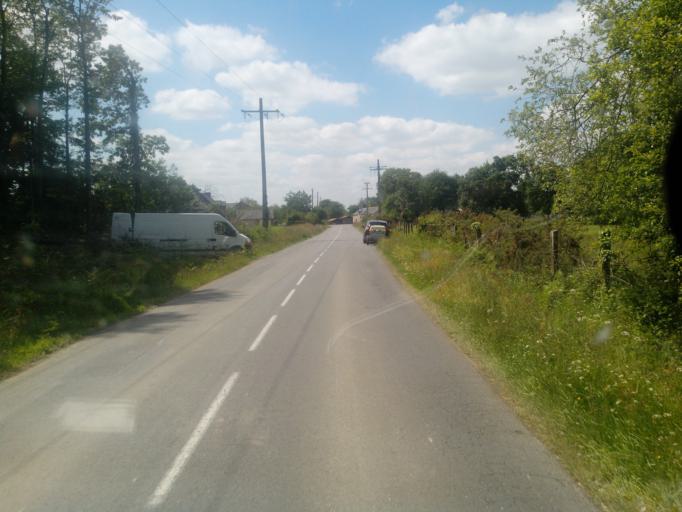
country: FR
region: Brittany
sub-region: Departement d'Ille-et-Vilaine
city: Saint-Marc-le-Blanc
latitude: 48.3701
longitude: -1.4387
